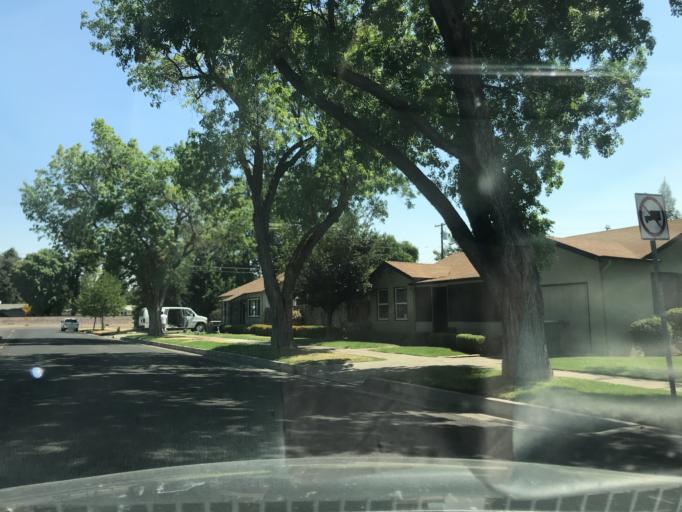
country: US
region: California
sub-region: Merced County
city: Merced
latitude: 37.3130
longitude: -120.4950
